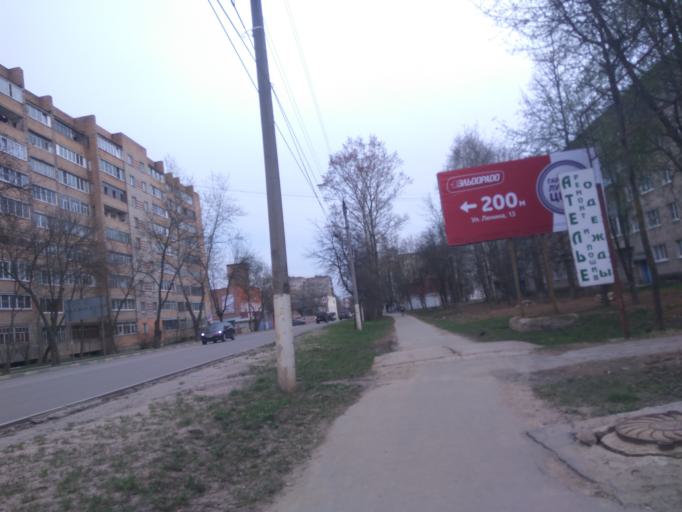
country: RU
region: Vladimir
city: Aleksandrov
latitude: 56.3999
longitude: 38.7135
